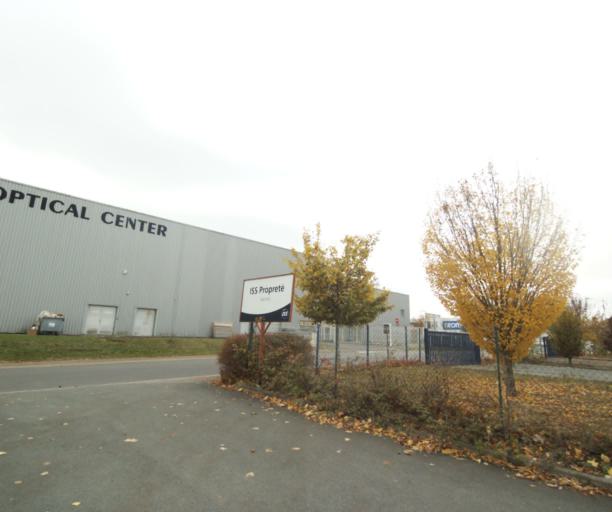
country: FR
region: Poitou-Charentes
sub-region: Departement de la Charente-Maritime
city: Saintes
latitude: 45.7500
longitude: -0.6739
